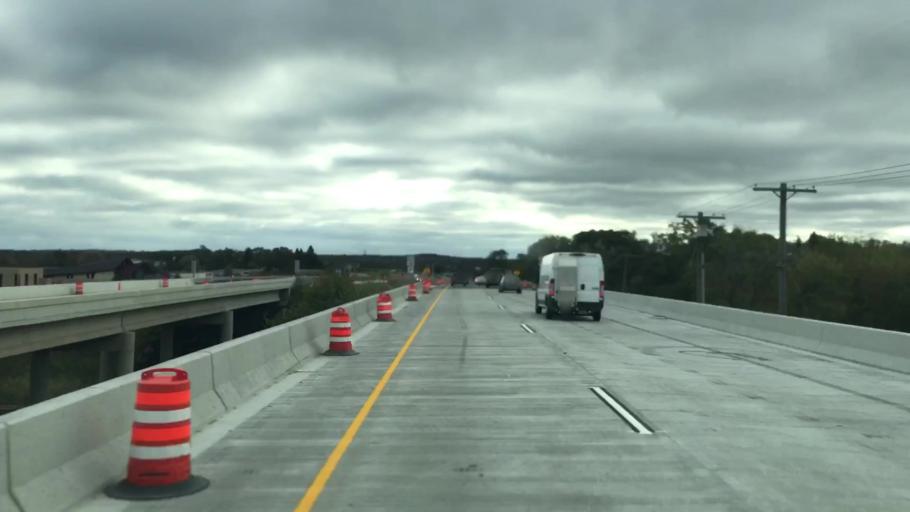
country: US
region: Wisconsin
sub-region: Waukesha County
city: Sussex
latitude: 43.0826
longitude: -88.1923
